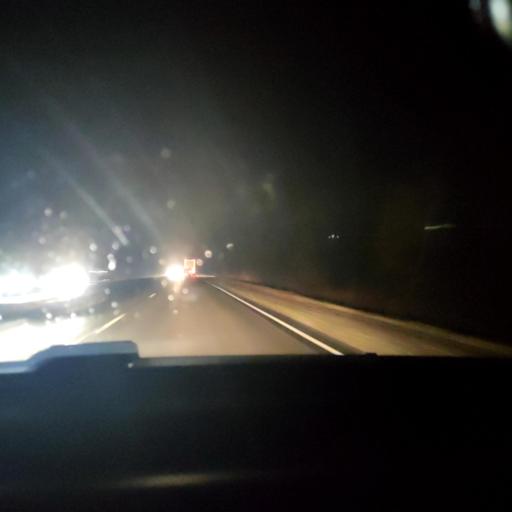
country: RU
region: Voronezj
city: Latnaya
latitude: 51.6324
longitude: 38.6663
